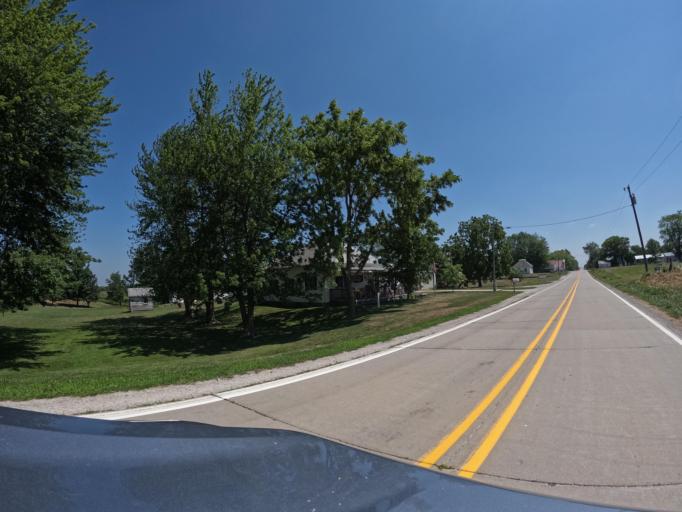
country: US
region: Iowa
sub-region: Keokuk County
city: Sigourney
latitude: 41.2648
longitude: -92.2523
